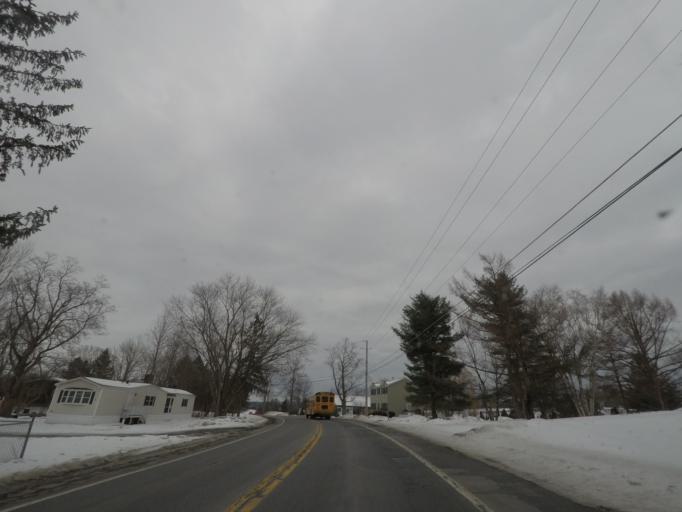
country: US
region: New York
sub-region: Saratoga County
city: Stillwater
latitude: 42.9540
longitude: -73.6696
